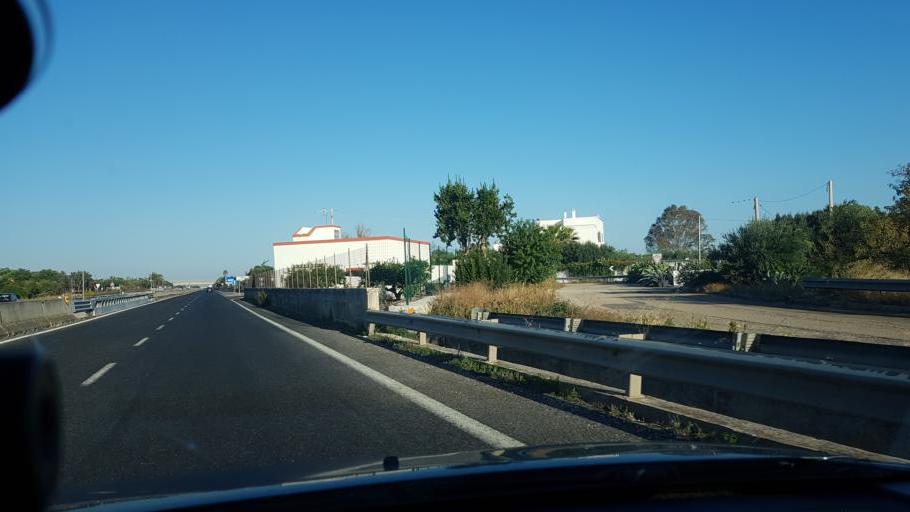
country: IT
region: Apulia
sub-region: Provincia di Bari
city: Monopoli
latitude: 40.9271
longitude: 17.3088
